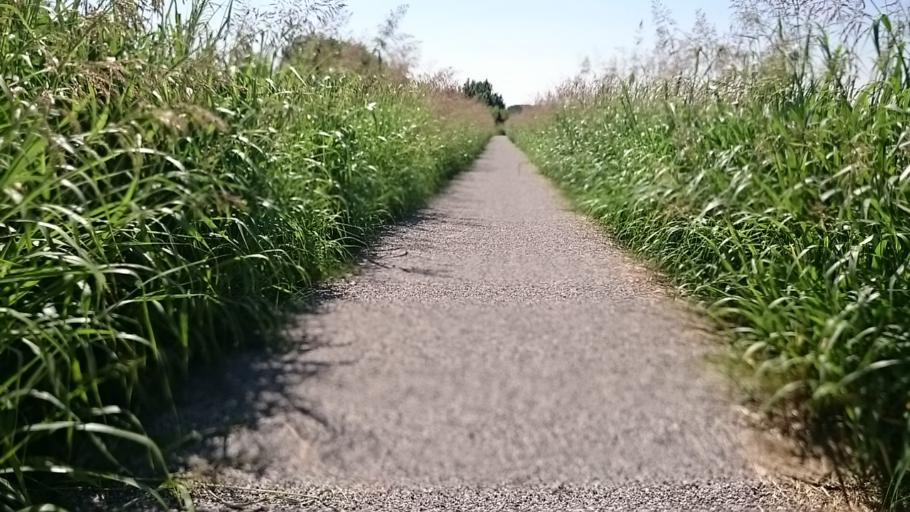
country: IT
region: Veneto
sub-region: Provincia di Padova
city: Cervarese Santa Croce
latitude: 45.4221
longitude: 11.7015
